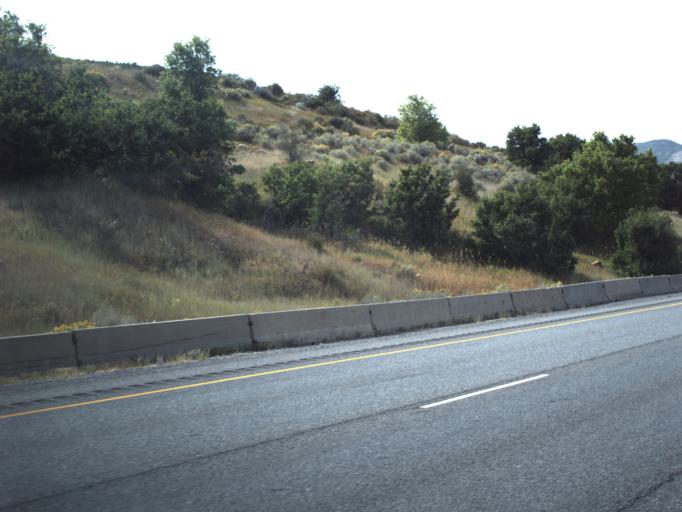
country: US
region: Utah
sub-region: Summit County
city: Summit Park
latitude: 40.7457
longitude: -111.6923
